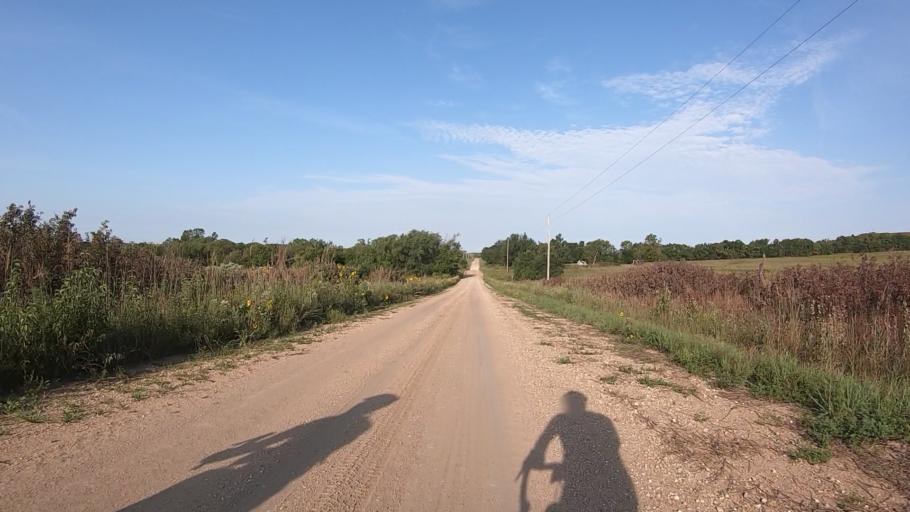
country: US
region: Kansas
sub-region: Marshall County
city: Blue Rapids
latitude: 39.6533
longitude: -96.8500
